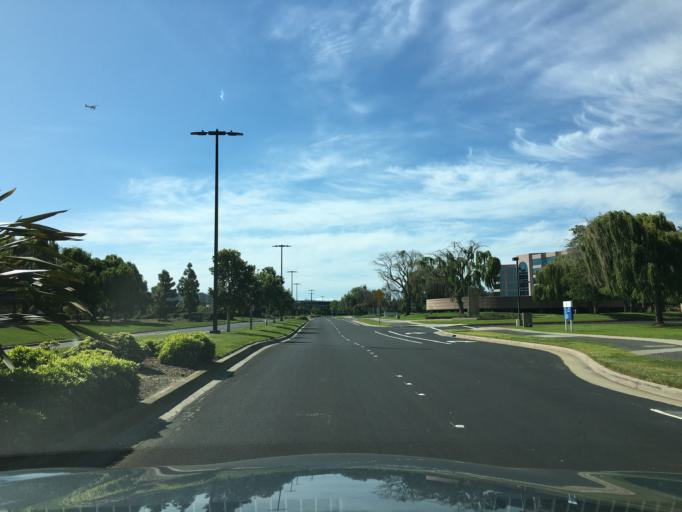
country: US
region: California
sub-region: San Mateo County
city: Redwood Shores
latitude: 37.5192
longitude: -122.2534
